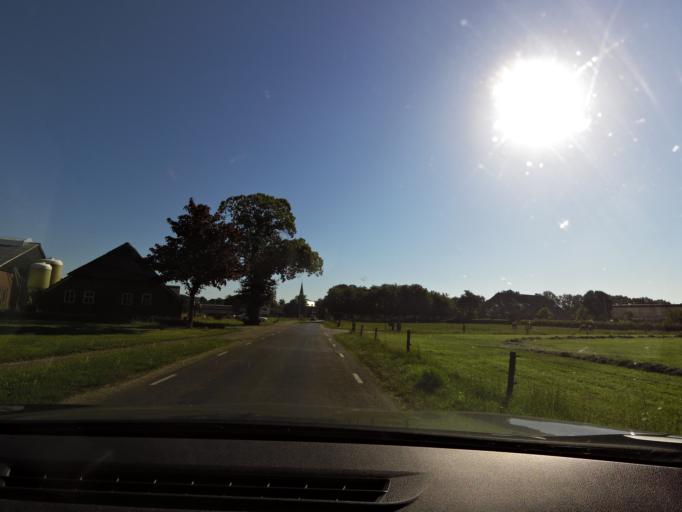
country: NL
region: Overijssel
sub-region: Gemeente Deventer
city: Schalkhaar
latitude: 52.2748
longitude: 6.2666
